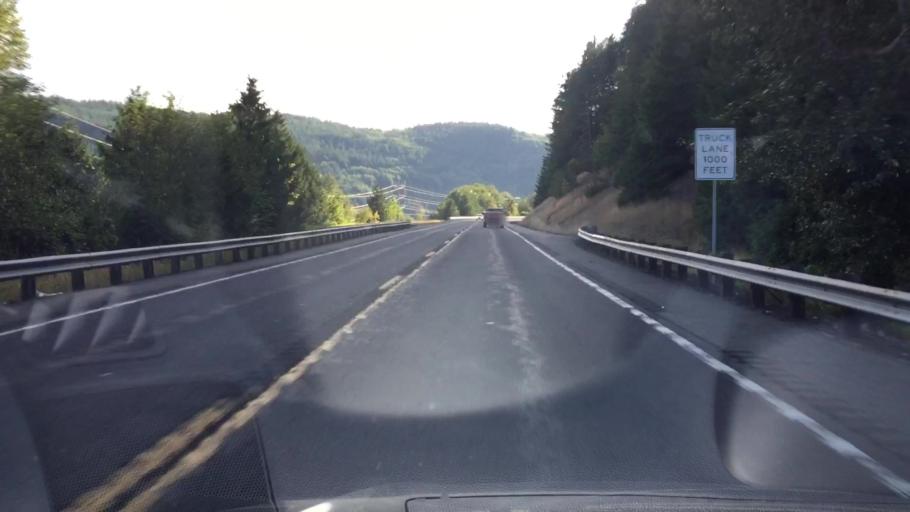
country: US
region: Washington
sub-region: Lewis County
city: Morton
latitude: 46.5464
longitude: -122.3228
